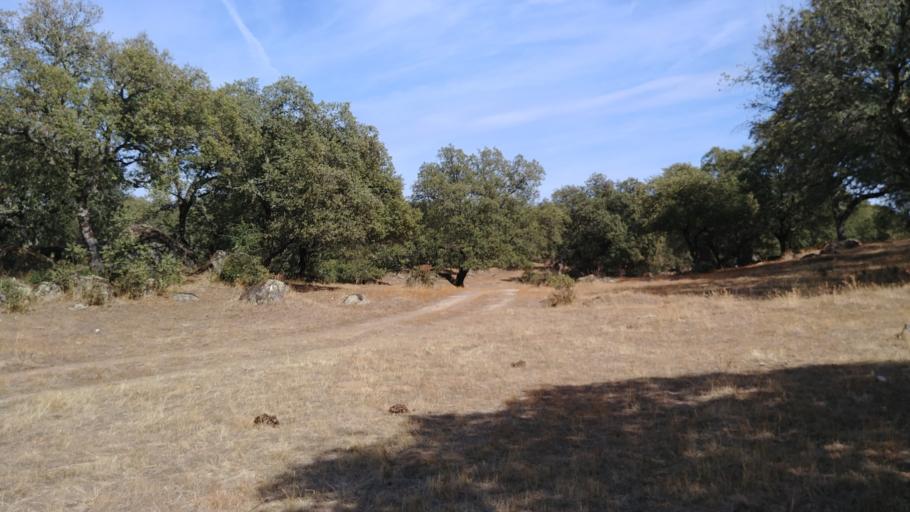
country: ES
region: Castille-La Mancha
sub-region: Province of Toledo
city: Navalcan
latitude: 40.0510
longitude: -5.1366
